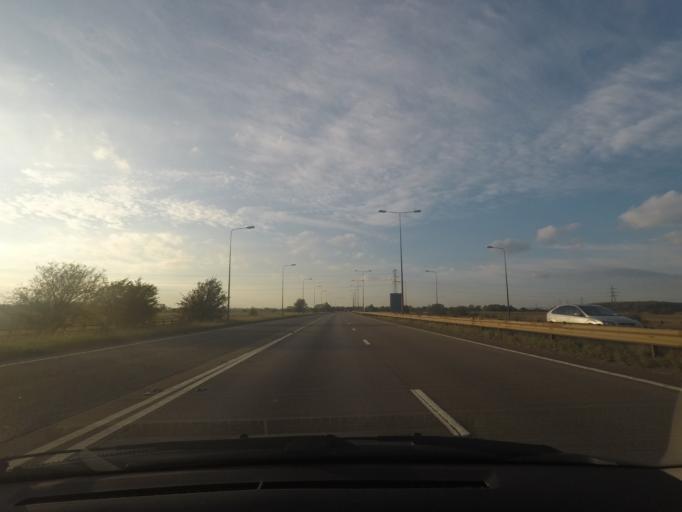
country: GB
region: England
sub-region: North East Lincolnshire
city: Great Coates
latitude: 53.5841
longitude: -0.1448
